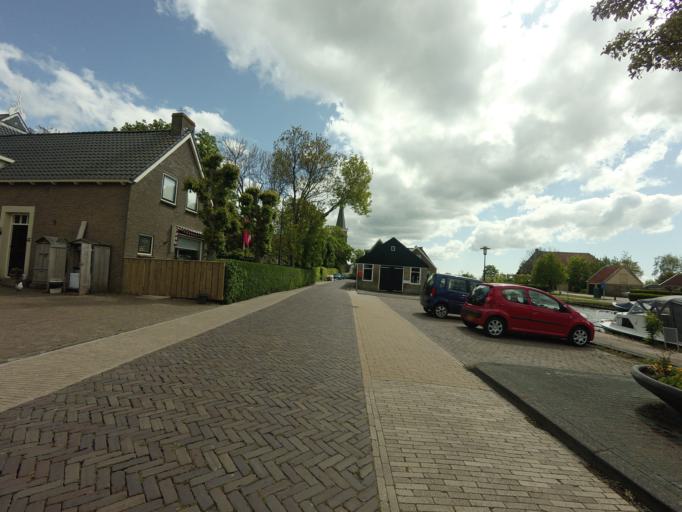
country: NL
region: Friesland
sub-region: Sudwest Fryslan
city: Bolsward
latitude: 53.0875
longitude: 5.5467
